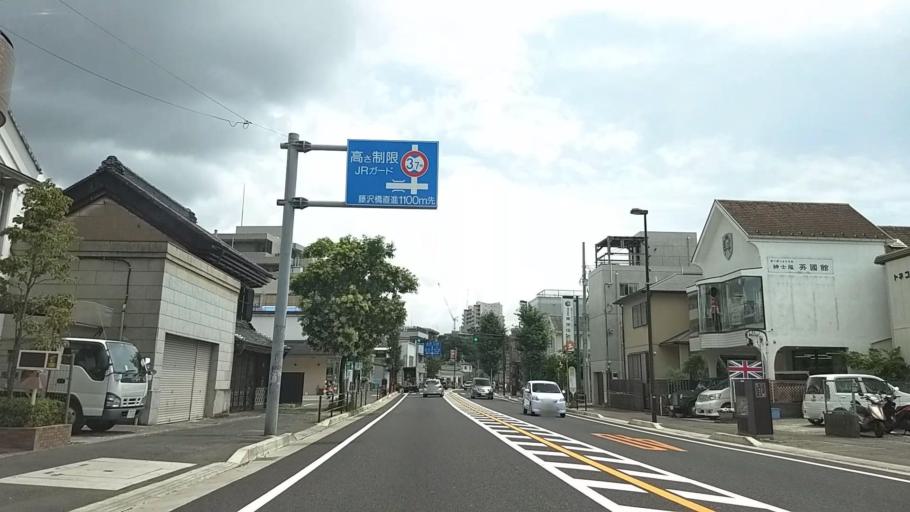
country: JP
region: Kanagawa
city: Fujisawa
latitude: 35.3469
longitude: 139.4850
